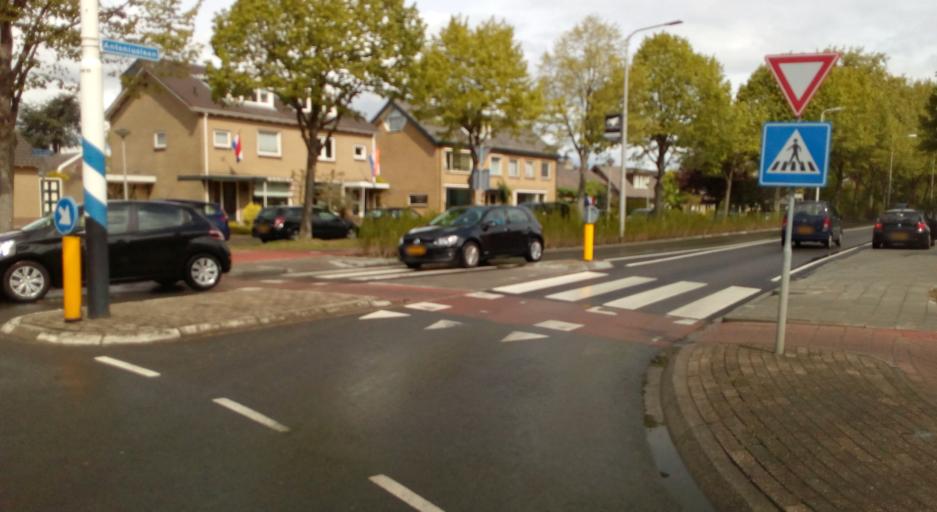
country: NL
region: South Holland
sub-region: Gemeente Hendrik-Ido-Ambacht
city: Hendrik-Ido-Ambacht
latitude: 51.8465
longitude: 4.6466
